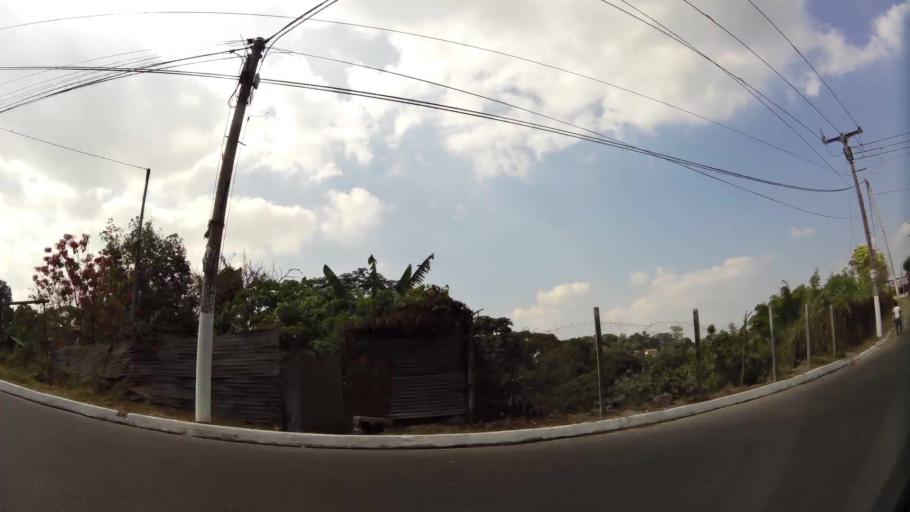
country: SV
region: San Salvador
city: Delgado
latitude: 13.7196
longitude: -89.1635
